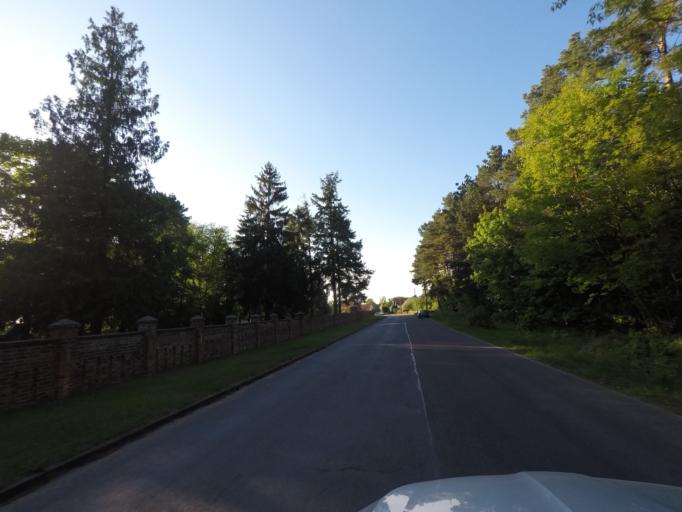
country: DE
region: Brandenburg
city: Bad Freienwalde
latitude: 52.8302
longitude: 14.0069
